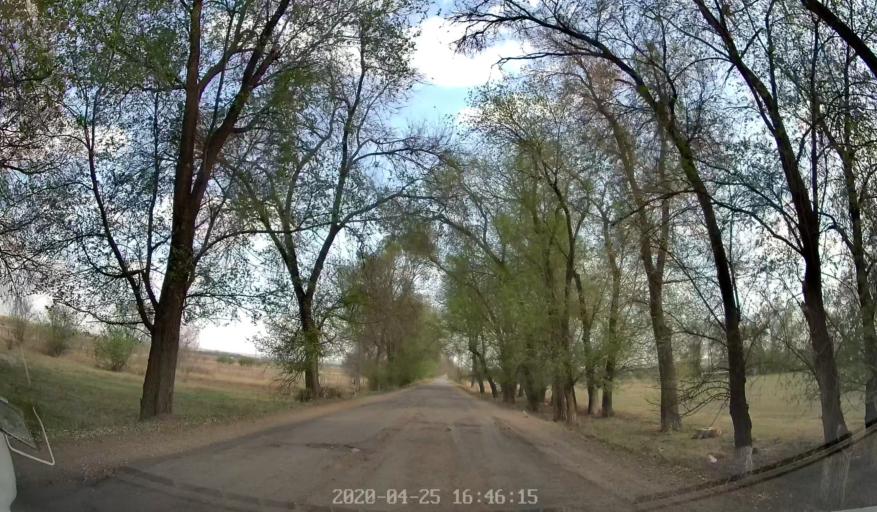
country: MD
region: Chisinau
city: Vadul lui Voda
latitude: 47.1415
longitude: 29.0677
